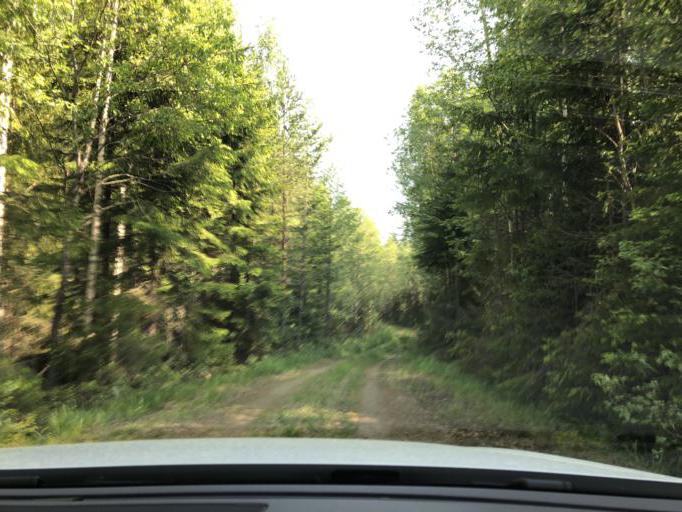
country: SE
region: Dalarna
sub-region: Avesta Kommun
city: Horndal
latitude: 60.2192
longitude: 16.5173
